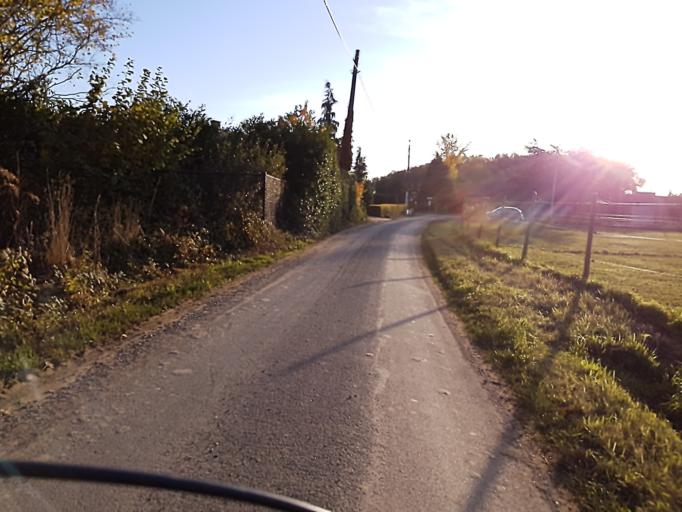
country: BE
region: Flanders
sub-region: Provincie Antwerpen
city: Bonheiden
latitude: 51.0540
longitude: 4.5817
